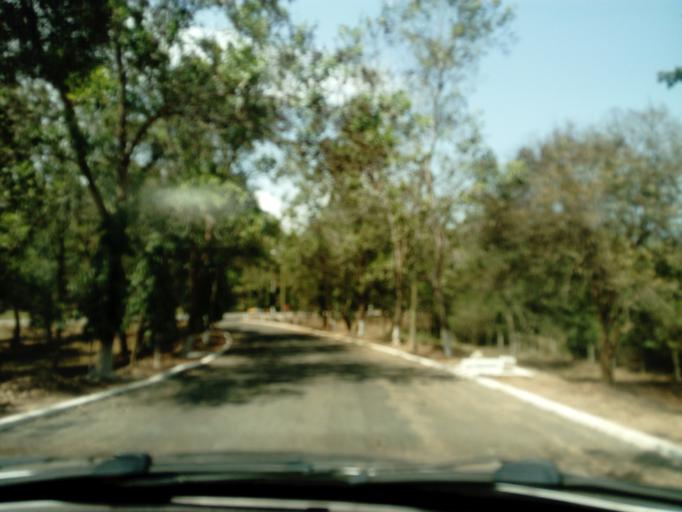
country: GH
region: Central
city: Cape Coast
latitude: 5.1139
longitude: -1.2849
